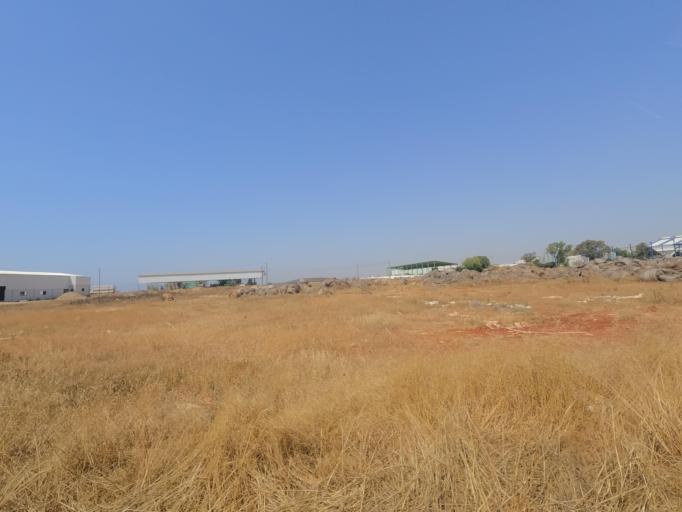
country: CY
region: Ammochostos
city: Avgorou
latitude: 35.0162
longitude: 33.8043
